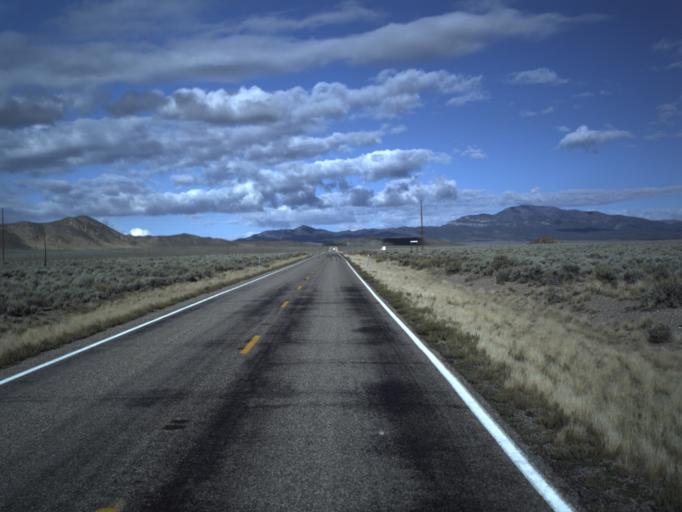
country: US
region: Utah
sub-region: Beaver County
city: Milford
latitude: 38.4129
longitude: -113.0724
